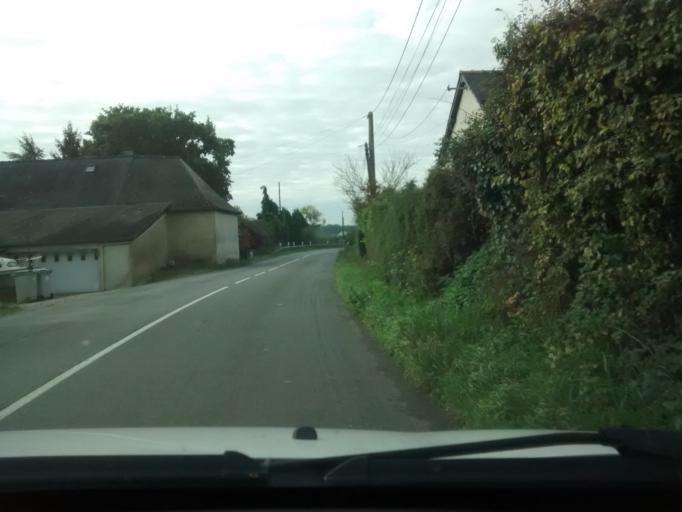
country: FR
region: Brittany
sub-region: Departement d'Ille-et-Vilaine
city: Vezin-le-Coquet
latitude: 48.0821
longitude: -1.7565
